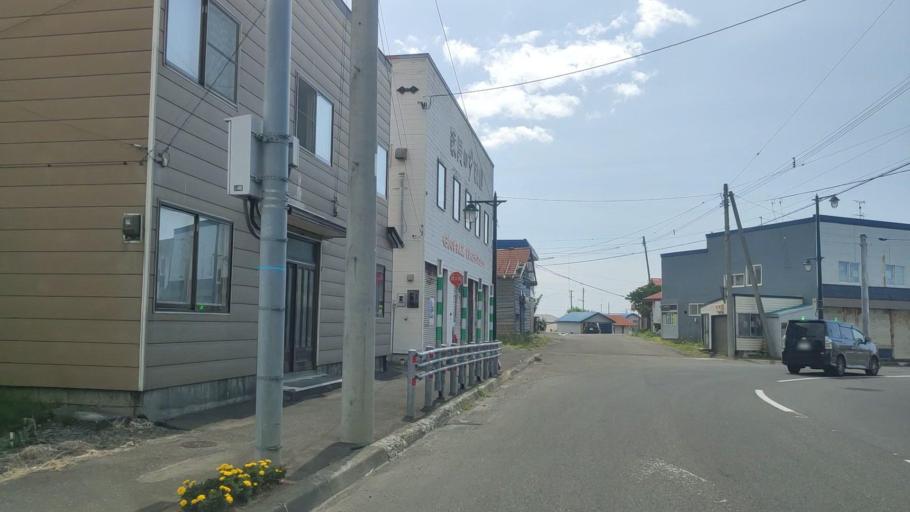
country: JP
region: Hokkaido
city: Makubetsu
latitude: 44.7219
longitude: 141.7964
